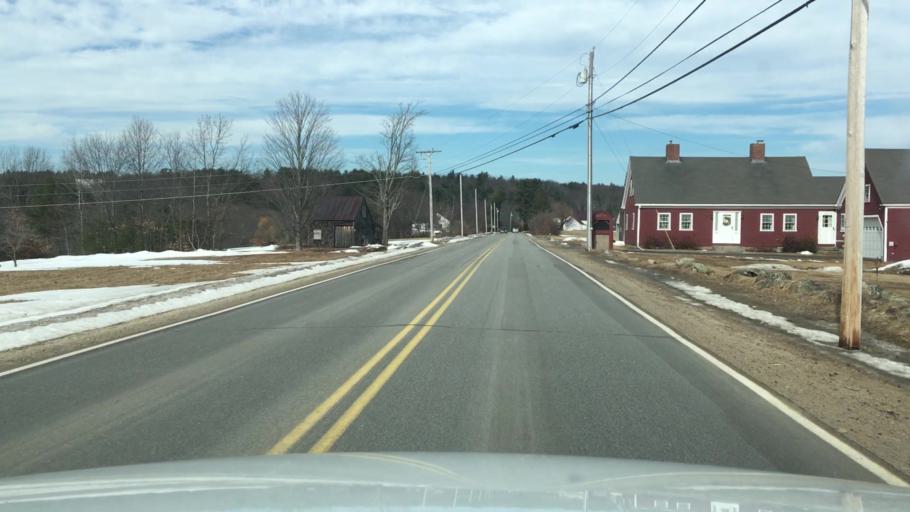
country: US
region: Maine
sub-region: York County
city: Springvale
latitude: 43.4953
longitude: -70.8108
